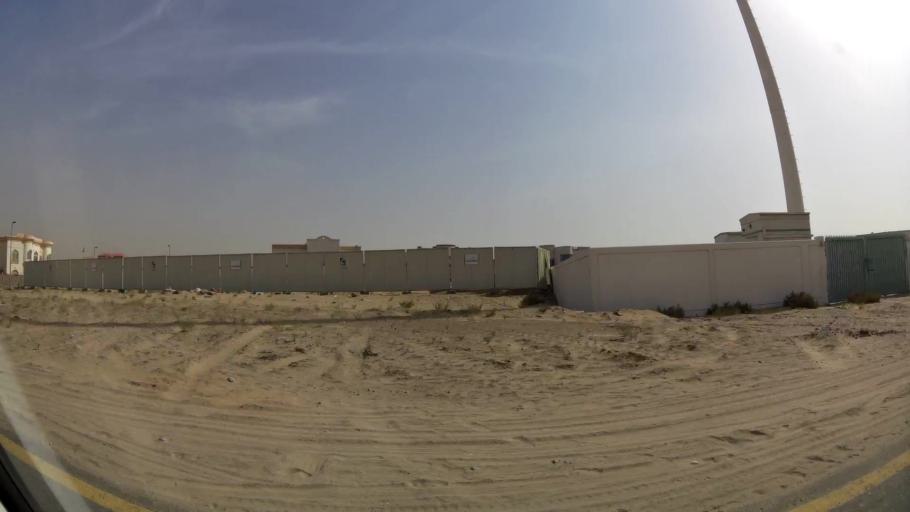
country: AE
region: Ash Shariqah
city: Sharjah
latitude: 25.2601
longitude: 55.4594
